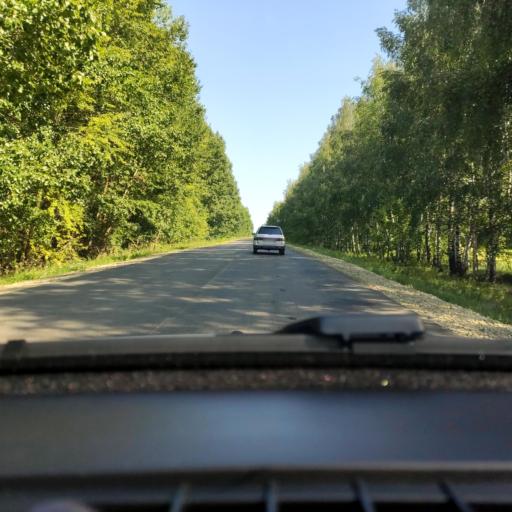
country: RU
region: Voronezj
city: Pereleshinskiy
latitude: 51.6418
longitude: 40.3051
